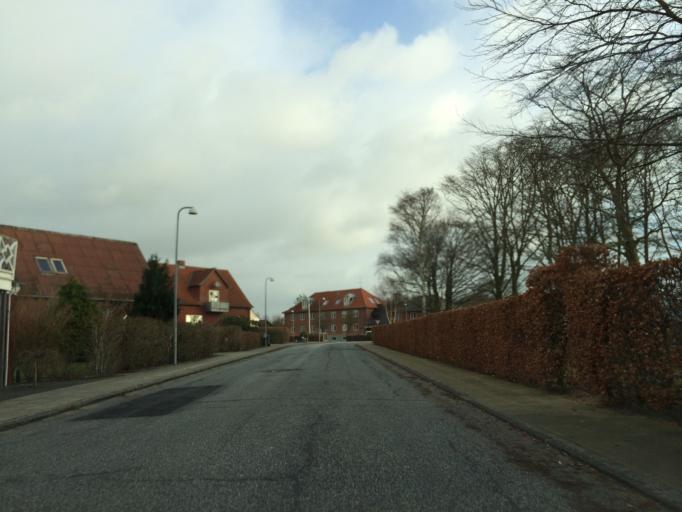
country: DK
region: Central Jutland
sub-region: Herning Kommune
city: Vildbjerg
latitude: 56.1944
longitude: 8.7648
